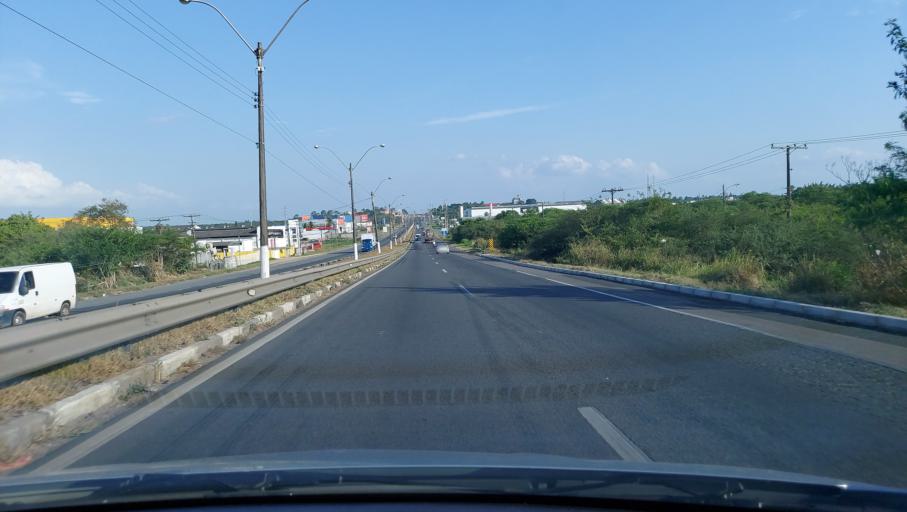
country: BR
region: Bahia
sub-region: Feira De Santana
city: Feira de Santana
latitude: -12.2845
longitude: -38.9192
